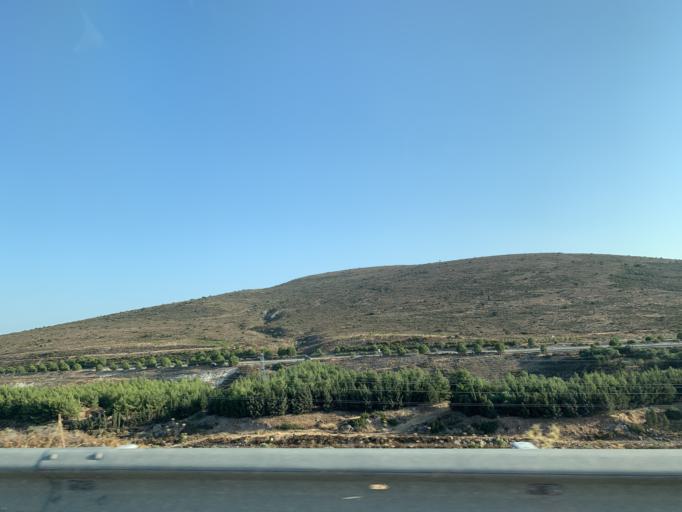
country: TR
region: Izmir
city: Alacati
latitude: 38.2762
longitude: 26.4103
